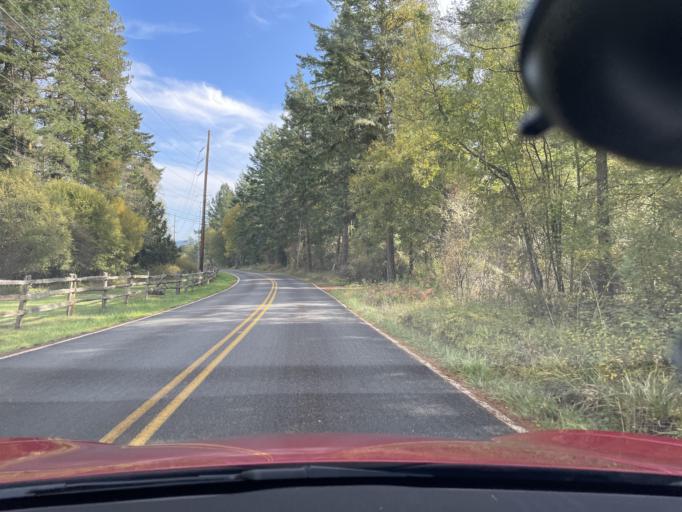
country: US
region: Washington
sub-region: San Juan County
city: Friday Harbor
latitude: 48.5182
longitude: -122.9864
